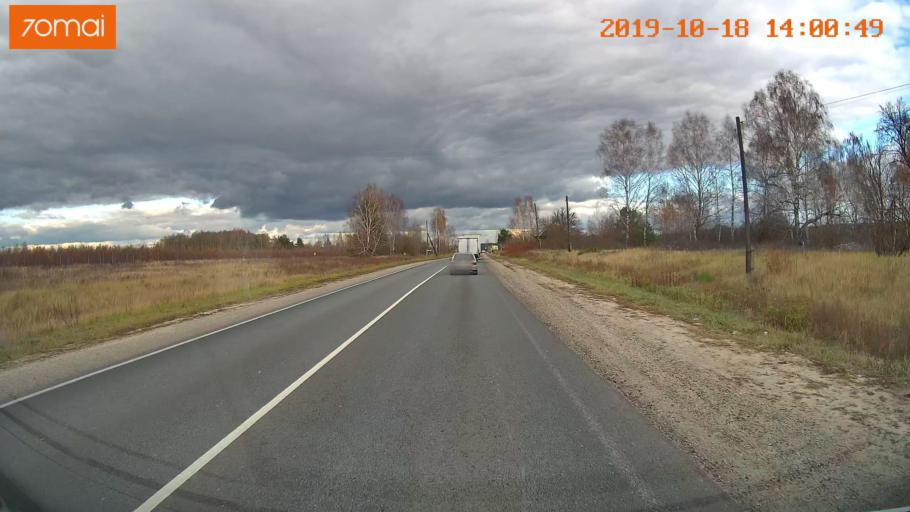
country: RU
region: Rjazan
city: Spas-Klepiki
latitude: 55.1035
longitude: 40.0809
